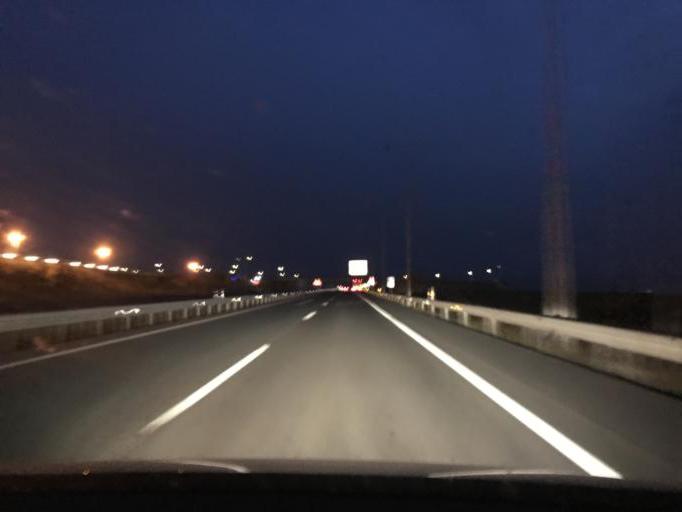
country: ES
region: Andalusia
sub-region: Provincia de Granada
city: Guadix
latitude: 37.3413
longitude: -3.0930
